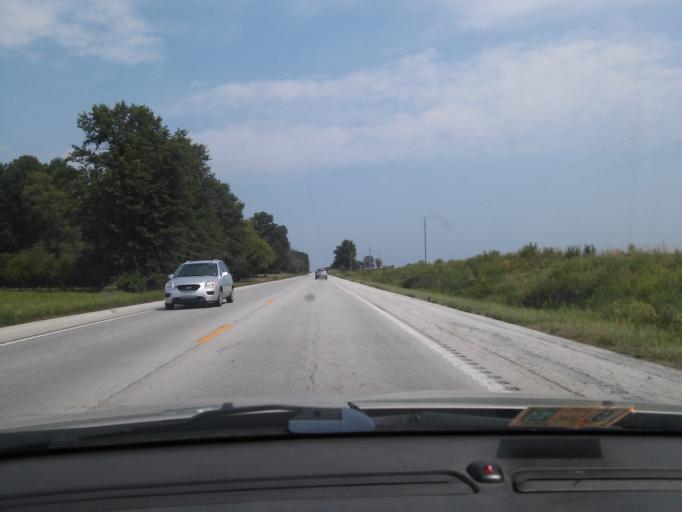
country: US
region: Missouri
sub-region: Montgomery County
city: Wellsville
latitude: 39.2088
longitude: -91.6465
